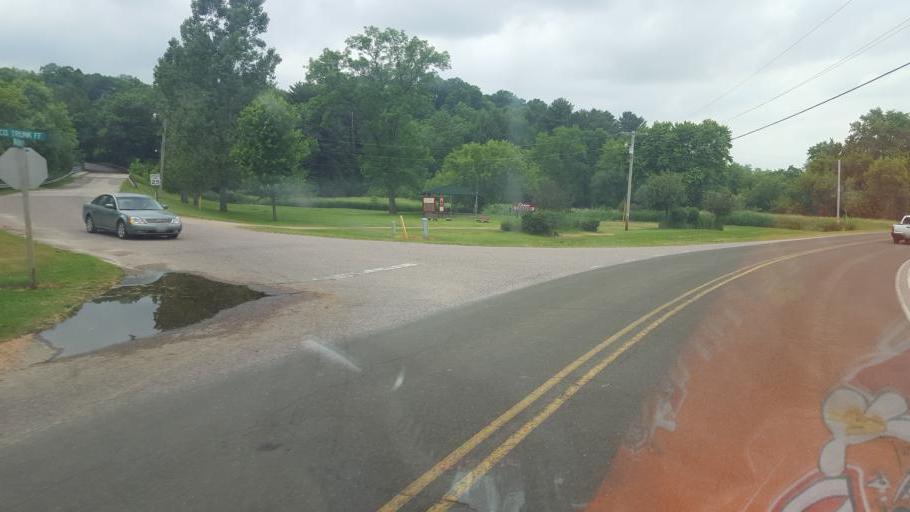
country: US
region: Wisconsin
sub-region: Juneau County
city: Elroy
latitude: 43.6530
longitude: -90.2262
